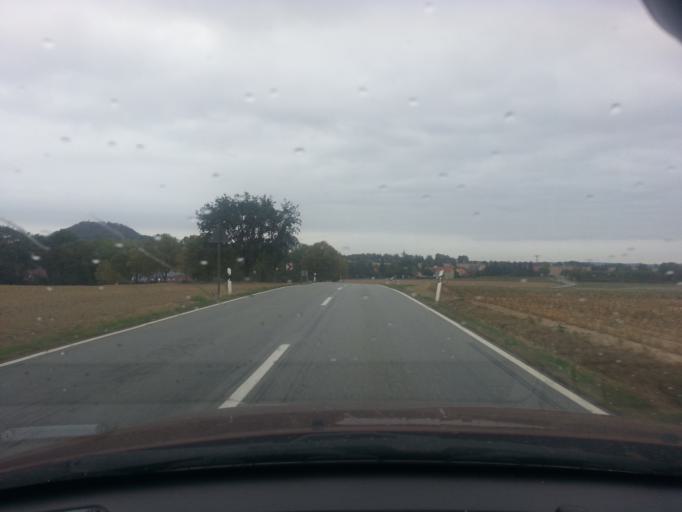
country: DE
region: Saxony
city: Markersdorf
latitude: 51.1110
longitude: 14.9155
